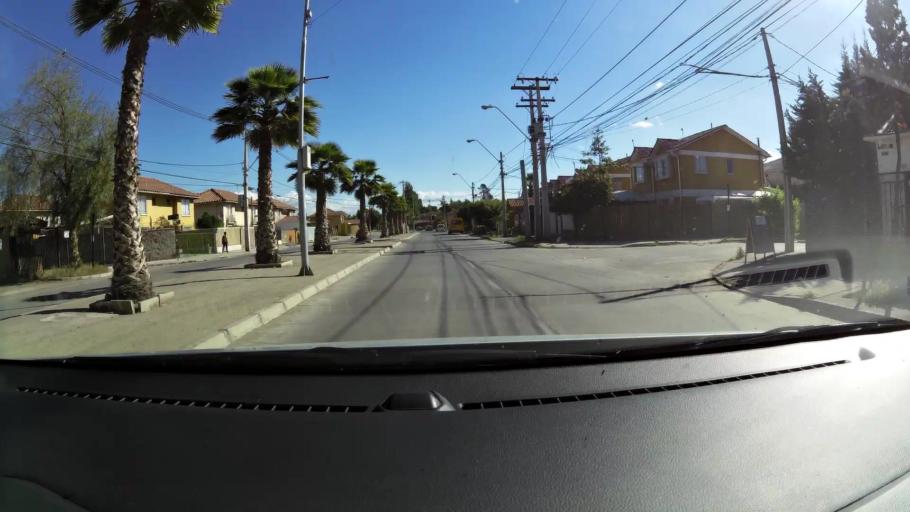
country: CL
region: Santiago Metropolitan
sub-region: Provincia de Maipo
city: San Bernardo
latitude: -33.5516
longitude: -70.7674
